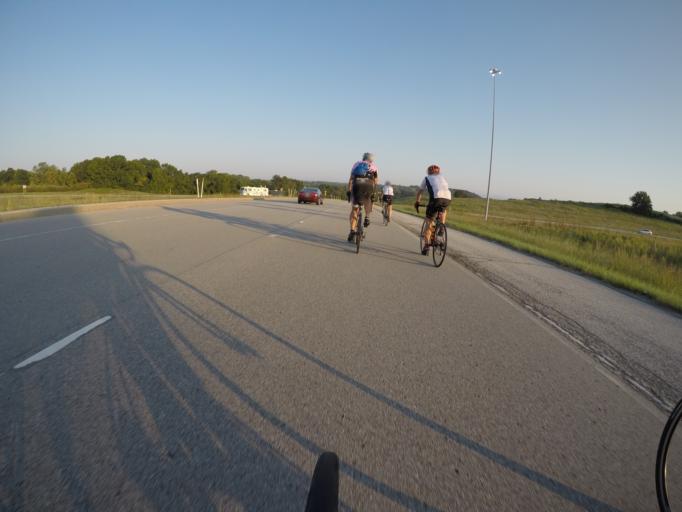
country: US
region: Missouri
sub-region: Platte County
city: Parkville
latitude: 39.1801
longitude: -94.7995
